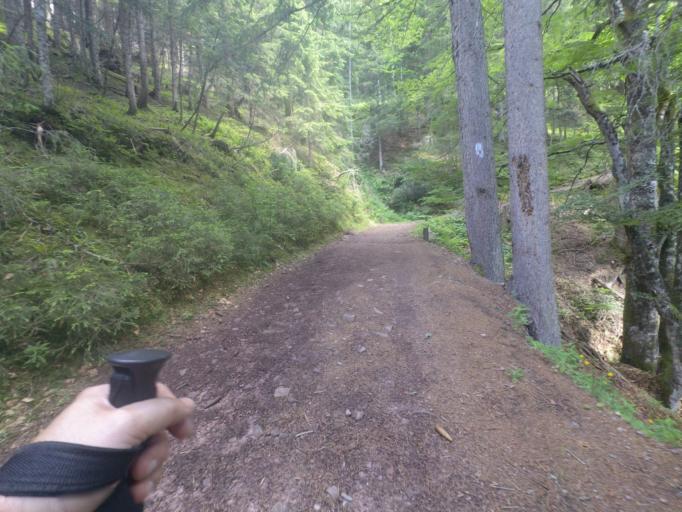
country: AT
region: Salzburg
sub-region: Politischer Bezirk Zell am See
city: Leogang
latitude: 47.4597
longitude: 12.7708
